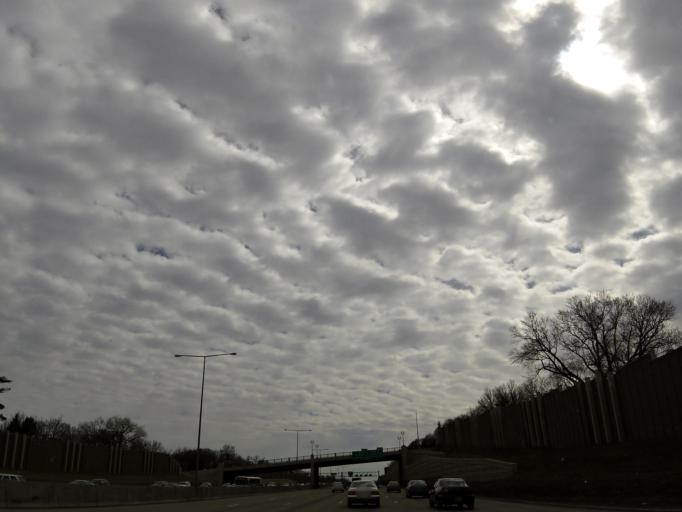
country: US
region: Minnesota
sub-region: Hennepin County
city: Richfield
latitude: 44.9142
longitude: -93.2752
